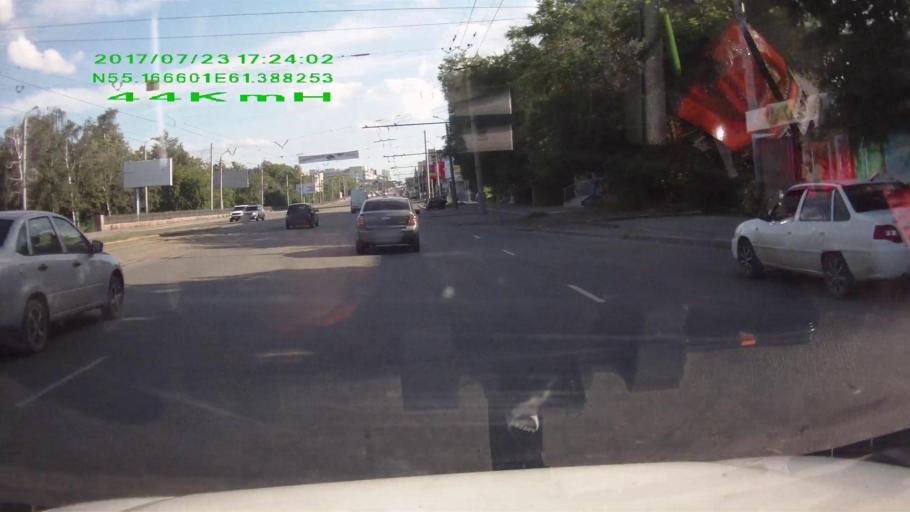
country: RU
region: Chelyabinsk
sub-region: Gorod Chelyabinsk
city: Chelyabinsk
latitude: 55.1663
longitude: 61.3883
